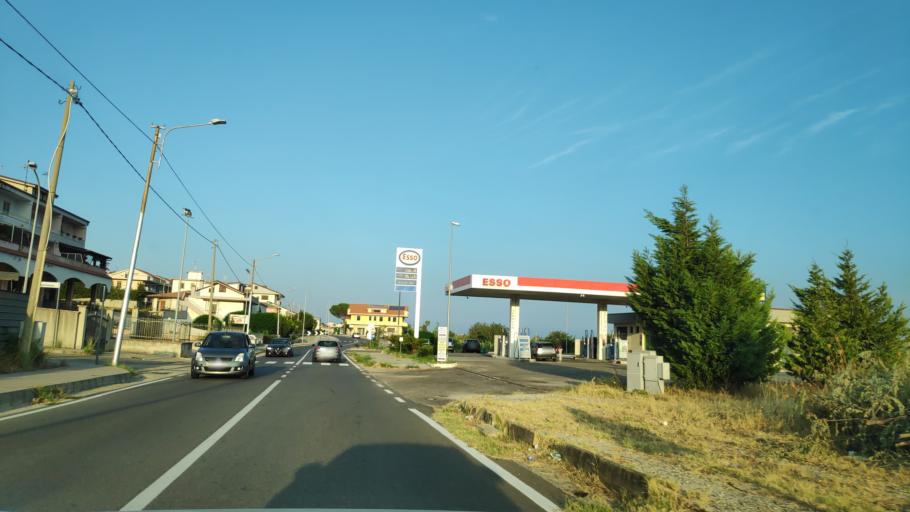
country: IT
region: Calabria
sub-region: Provincia di Catanzaro
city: Martelli-Laganosa
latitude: 38.6792
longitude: 16.5217
